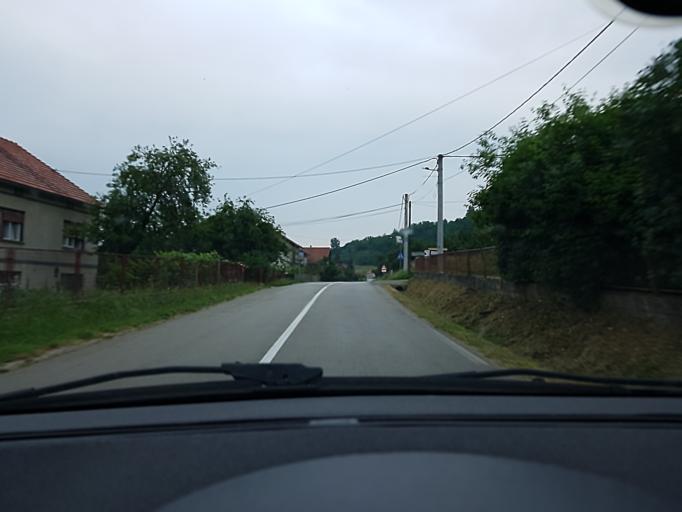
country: HR
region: Zagrebacka
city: Jakovlje
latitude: 45.9679
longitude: 15.8296
